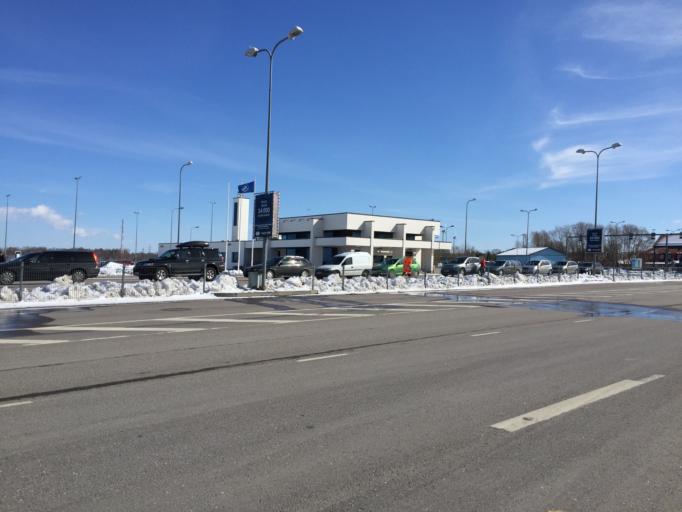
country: EE
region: Laeaene
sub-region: Lihula vald
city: Lihula
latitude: 58.5738
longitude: 23.5096
